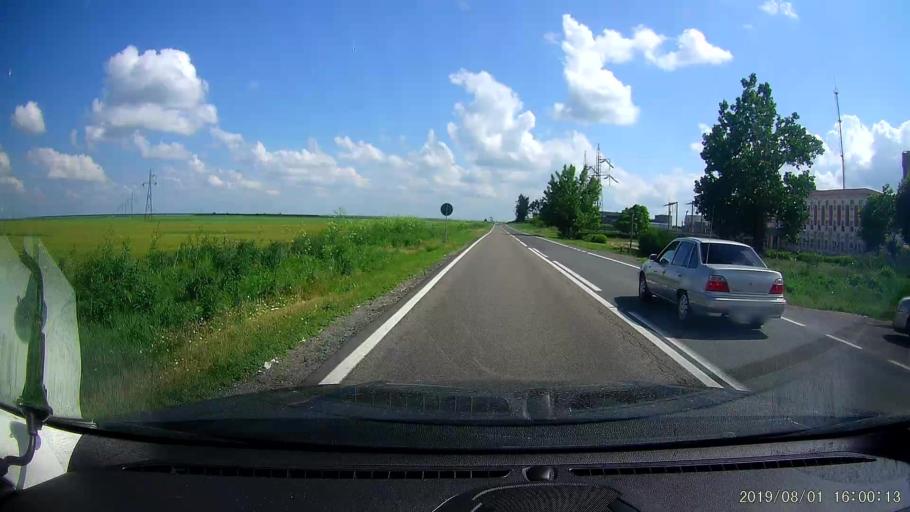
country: RO
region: Ialomita
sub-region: Comuna Ciulnita
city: Ciulnita
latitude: 44.5341
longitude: 27.3884
